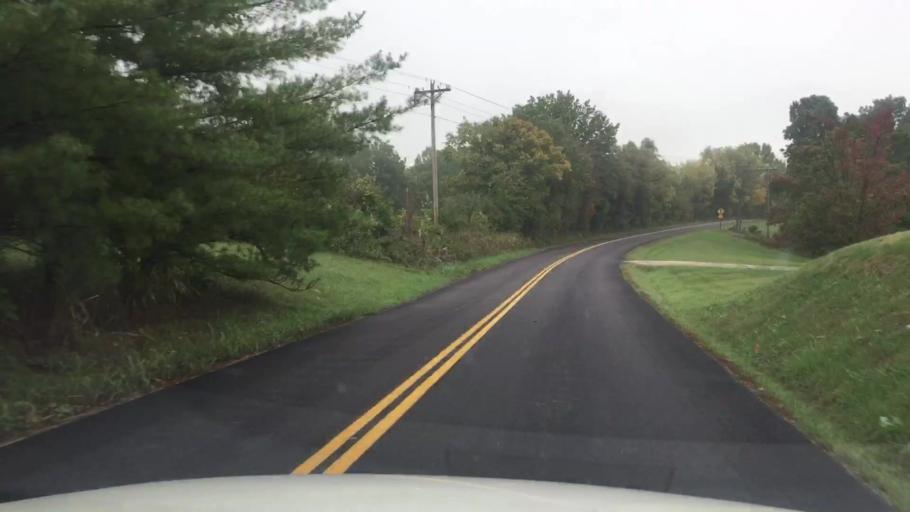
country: US
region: Missouri
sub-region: Boone County
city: Ashland
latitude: 38.8242
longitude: -92.3493
